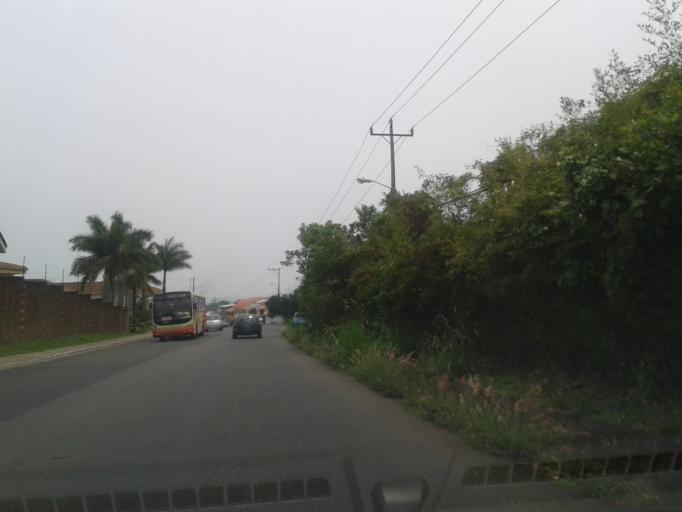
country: CR
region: Heredia
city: San Francisco
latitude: 9.9817
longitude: -84.1355
